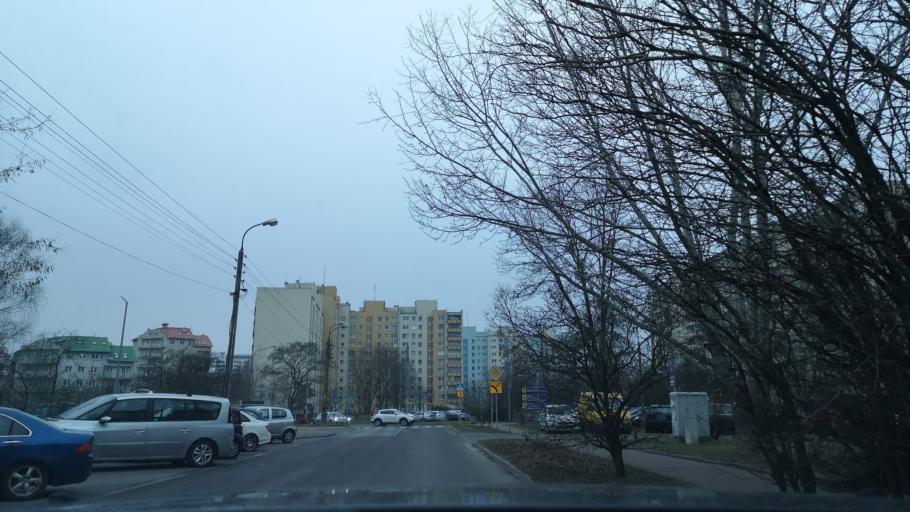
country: PL
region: Masovian Voivodeship
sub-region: Warszawa
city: Bemowo
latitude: 52.2418
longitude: 20.9193
